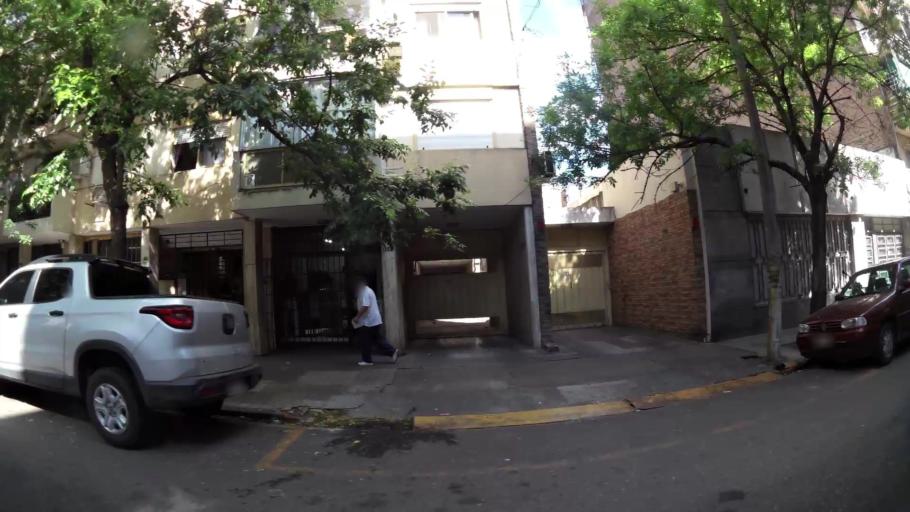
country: AR
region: Santa Fe
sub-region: Departamento de Rosario
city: Rosario
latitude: -32.9550
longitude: -60.6301
